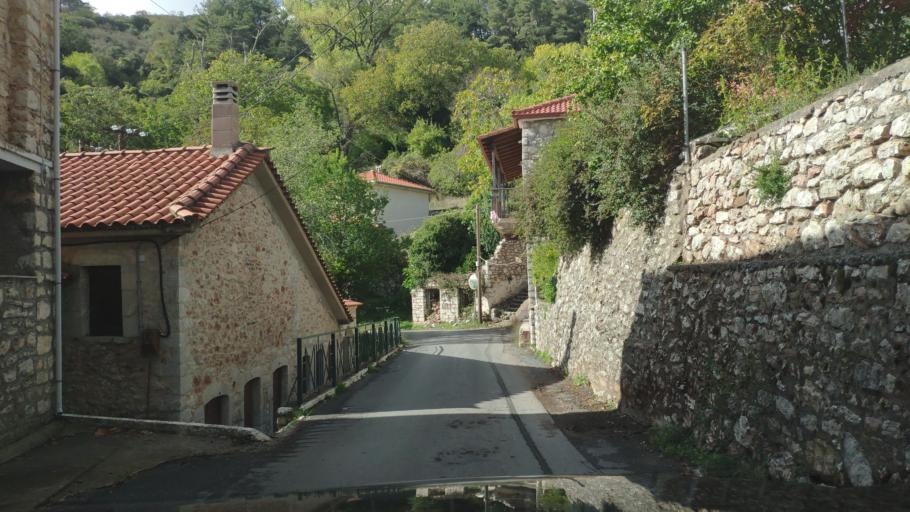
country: GR
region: Peloponnese
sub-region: Nomos Arkadias
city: Dimitsana
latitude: 37.5906
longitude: 22.0232
